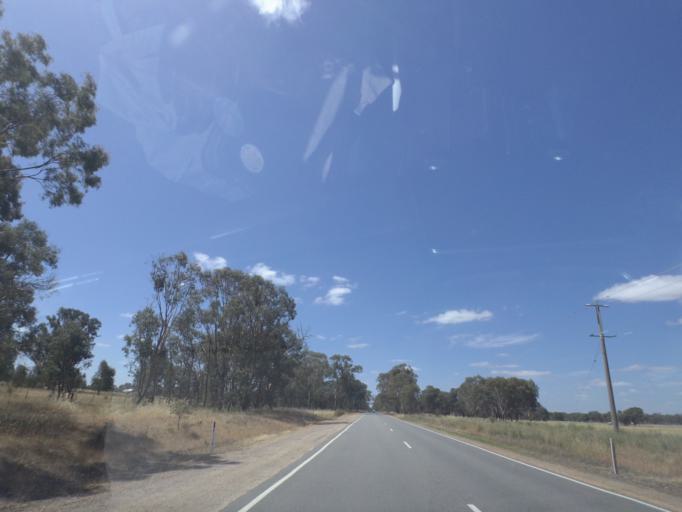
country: AU
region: Victoria
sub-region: Wangaratta
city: Wangaratta
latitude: -36.4237
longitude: 146.2590
